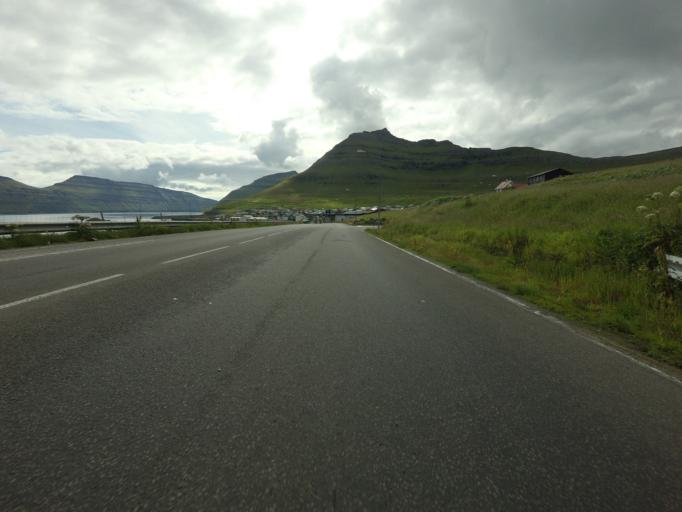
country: FO
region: Eysturoy
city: Eystur
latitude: 62.2143
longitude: -6.7165
